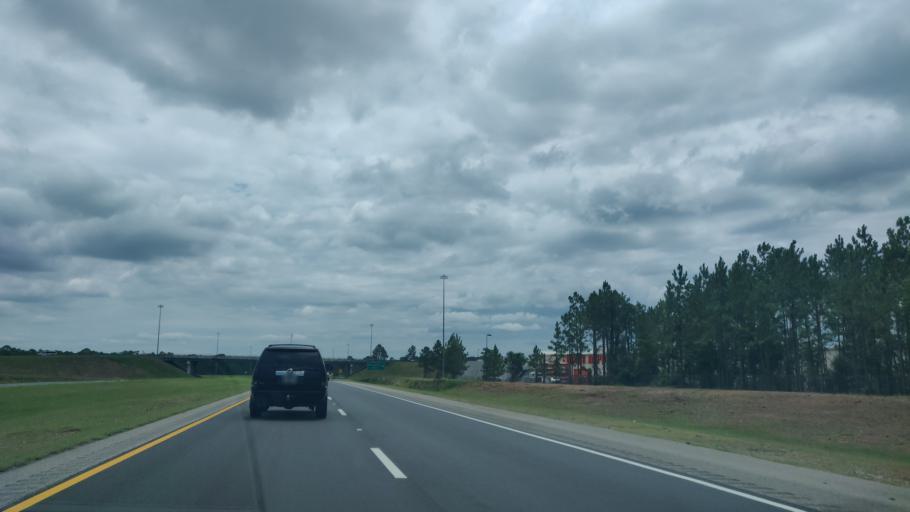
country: US
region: Georgia
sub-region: Dougherty County
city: Albany
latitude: 31.6182
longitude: -84.2073
